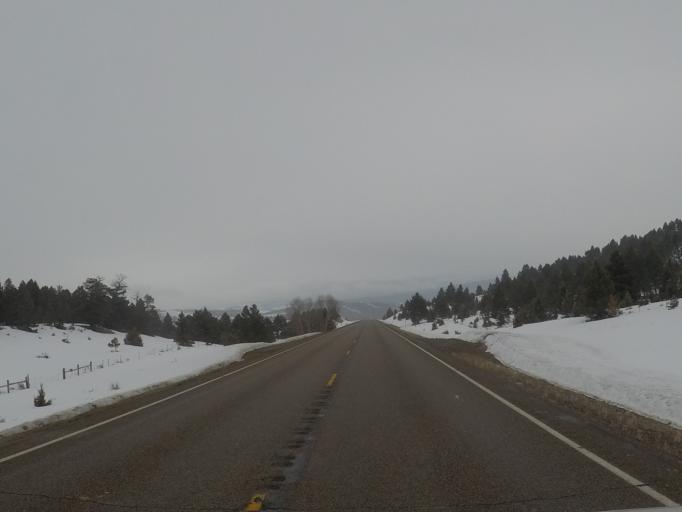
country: US
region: Montana
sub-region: Meagher County
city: White Sulphur Springs
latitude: 46.6392
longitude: -110.8597
